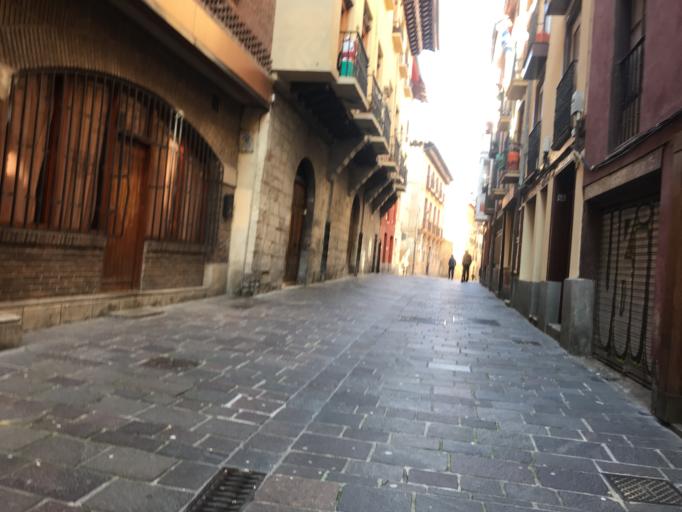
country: ES
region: Basque Country
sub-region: Provincia de Alava
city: Gasteiz / Vitoria
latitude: 42.8485
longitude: -2.6747
